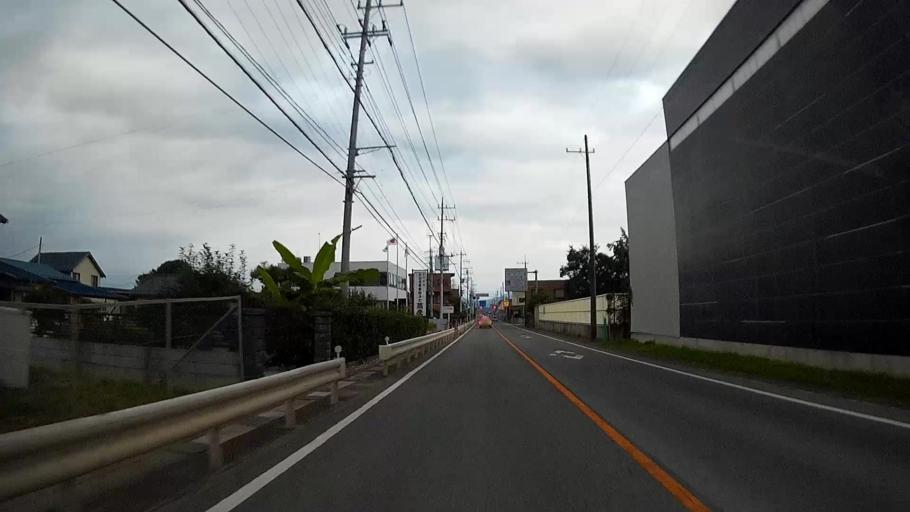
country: JP
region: Saitama
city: Chichibu
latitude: 35.9731
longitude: 139.0666
